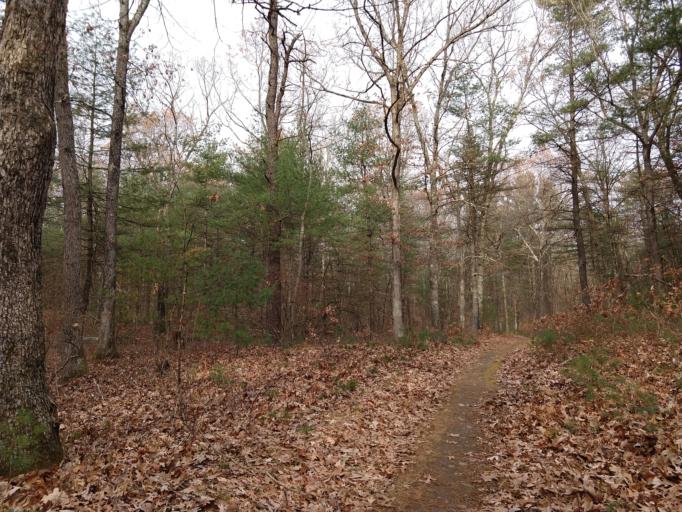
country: US
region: Massachusetts
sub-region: Middlesex County
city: Billerica
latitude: 42.5848
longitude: -71.3042
